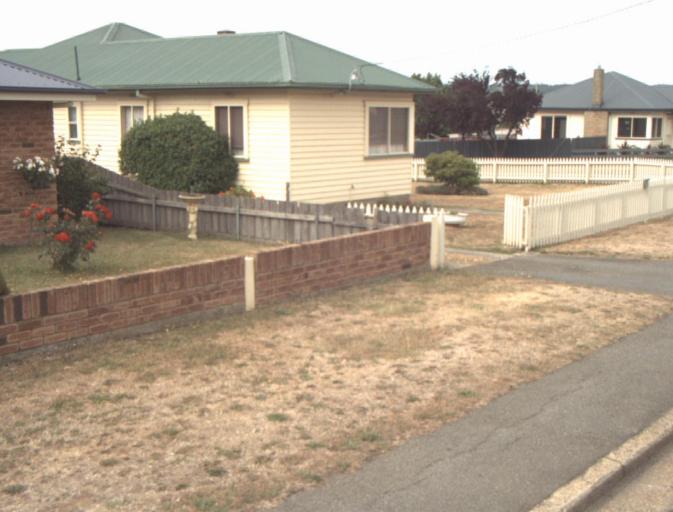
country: AU
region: Tasmania
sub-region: Launceston
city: Mayfield
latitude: -41.3893
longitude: 147.1314
